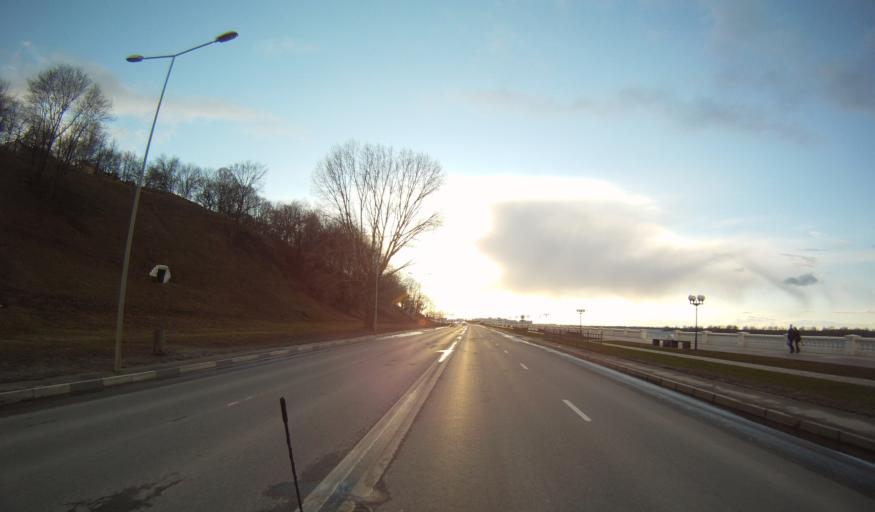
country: RU
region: Nizjnij Novgorod
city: Nizhniy Novgorod
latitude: 56.3312
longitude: 44.0187
